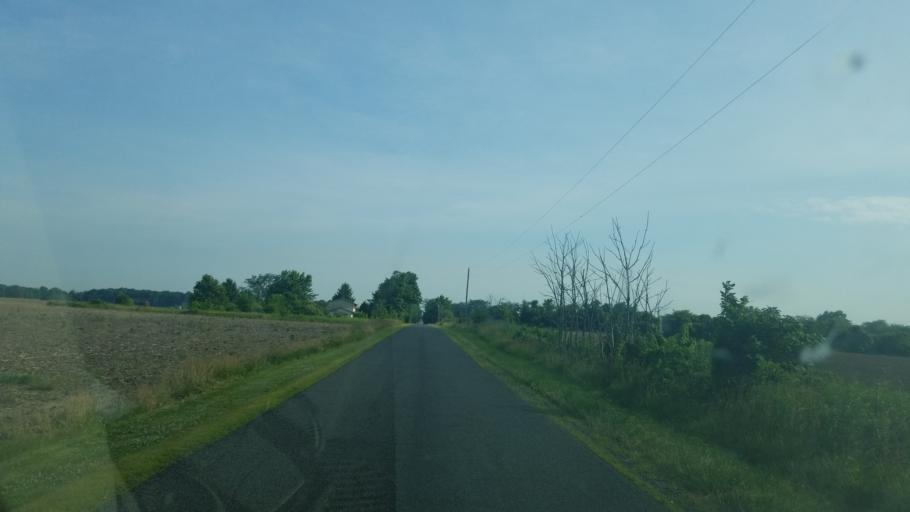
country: US
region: Ohio
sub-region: Hancock County
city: Arlington
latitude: 40.8488
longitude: -83.6702
